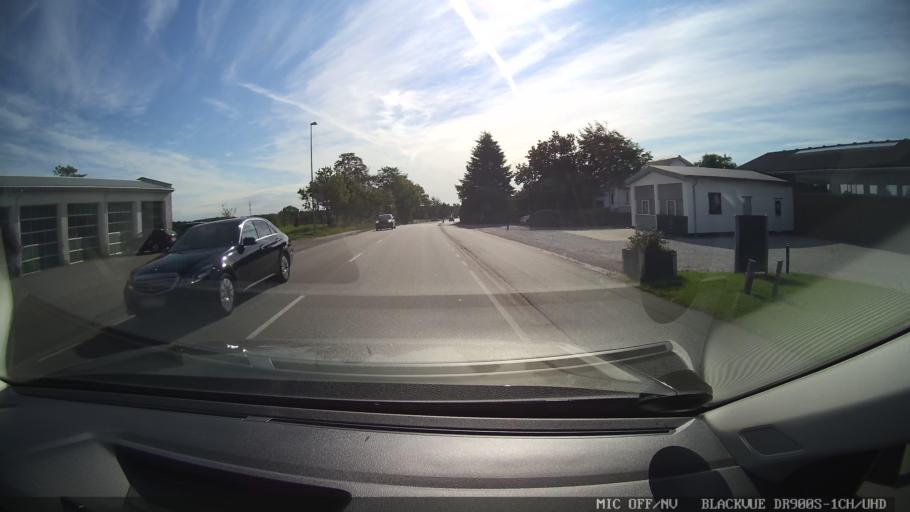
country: DK
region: North Denmark
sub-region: Mariagerfjord Kommune
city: Arden
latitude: 56.7715
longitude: 9.8506
